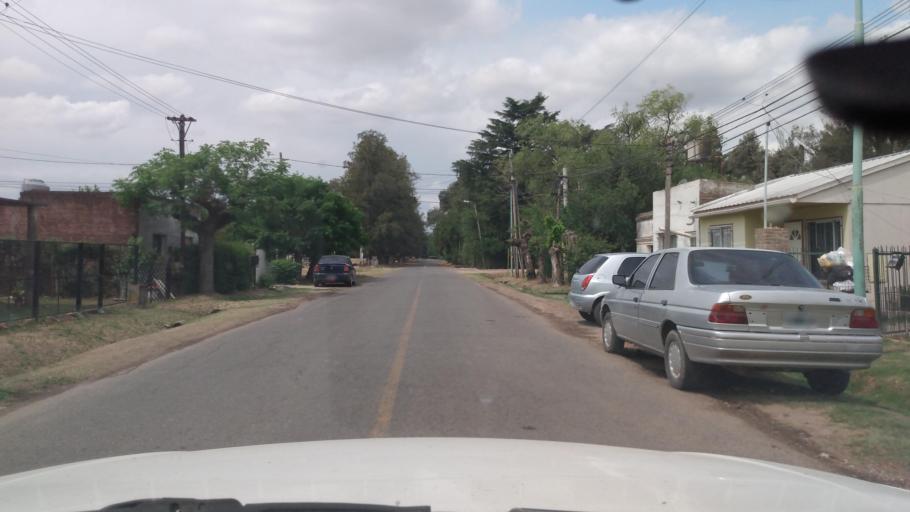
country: AR
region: Buenos Aires
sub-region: Partido de Lujan
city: Lujan
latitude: -34.5553
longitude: -59.2001
